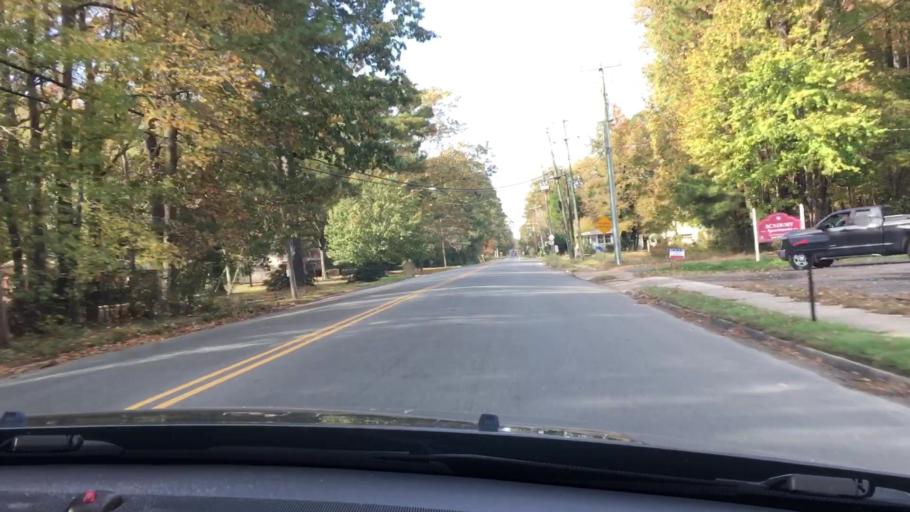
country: US
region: Virginia
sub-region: King William County
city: West Point
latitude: 37.5586
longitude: -76.8198
